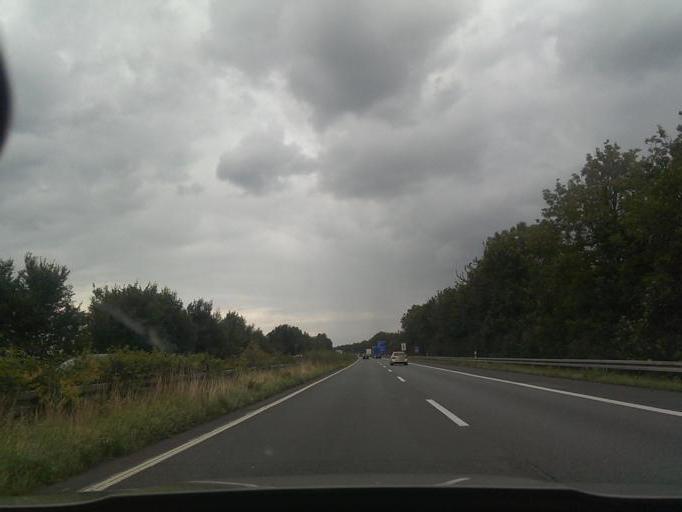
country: DE
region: North Rhine-Westphalia
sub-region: Regierungsbezirk Detmold
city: Paderborn
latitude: 51.7204
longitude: 8.7057
